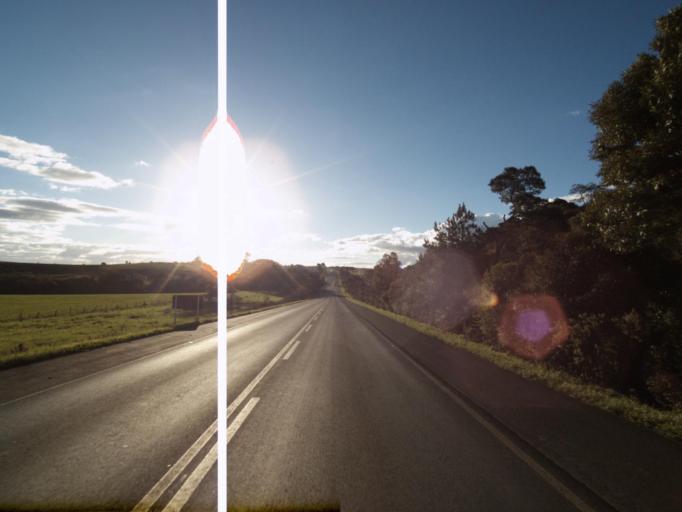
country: BR
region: Santa Catarina
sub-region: Campos Novos
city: Campos Novos
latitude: -27.3750
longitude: -51.2467
